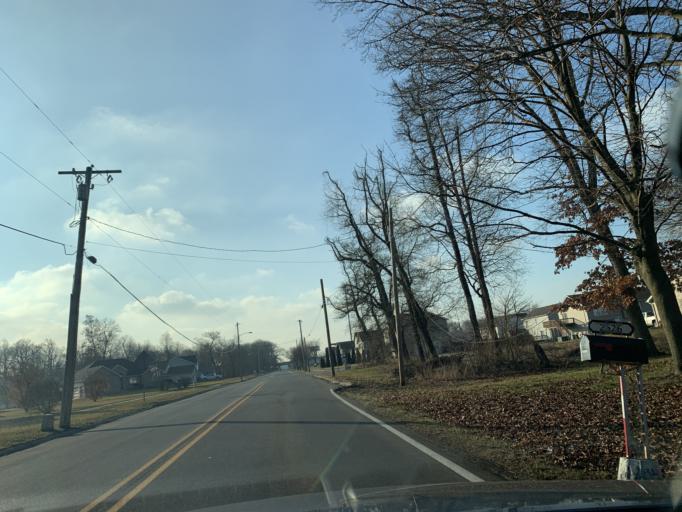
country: US
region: Indiana
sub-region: Porter County
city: Portage
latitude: 41.5789
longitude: -87.1535
